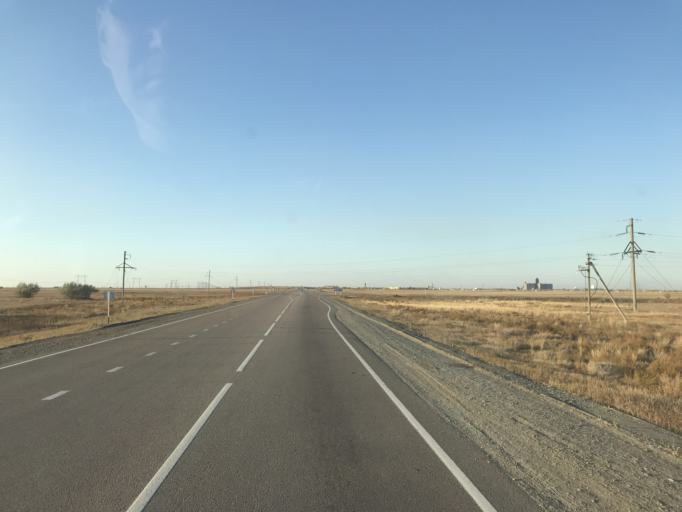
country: KZ
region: Pavlodar
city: Leninskiy
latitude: 52.2166
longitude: 76.7625
